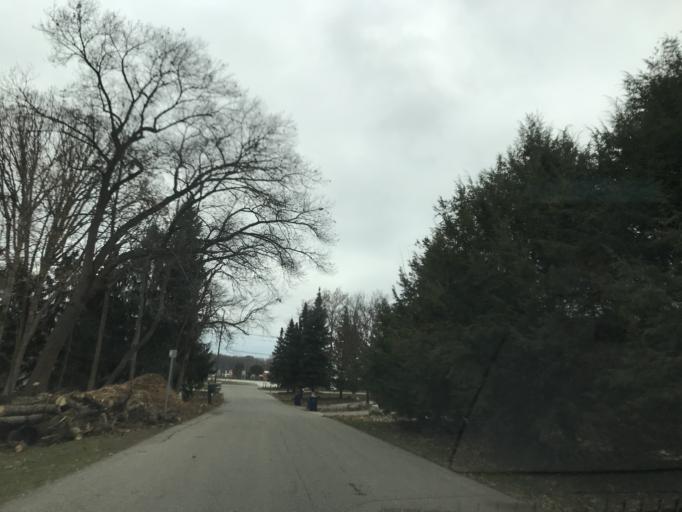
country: US
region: Michigan
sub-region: Oakland County
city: Bloomfield Hills
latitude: 42.6036
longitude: -83.2110
